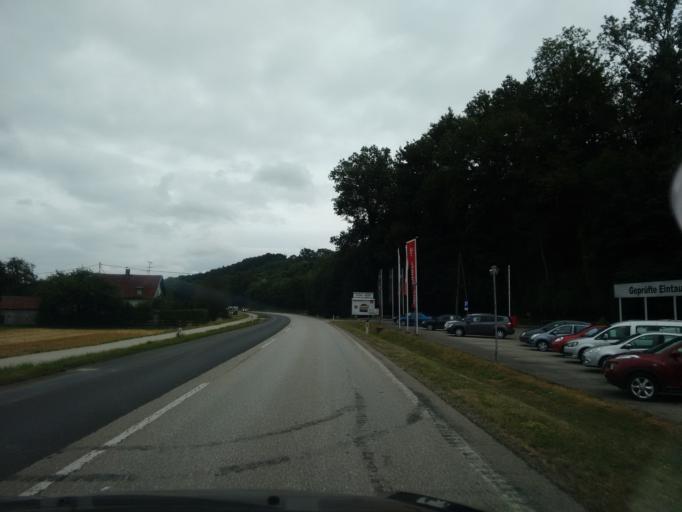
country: AT
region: Upper Austria
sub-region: Politischer Bezirk Grieskirchen
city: Grieskirchen
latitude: 48.2235
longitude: 13.8512
